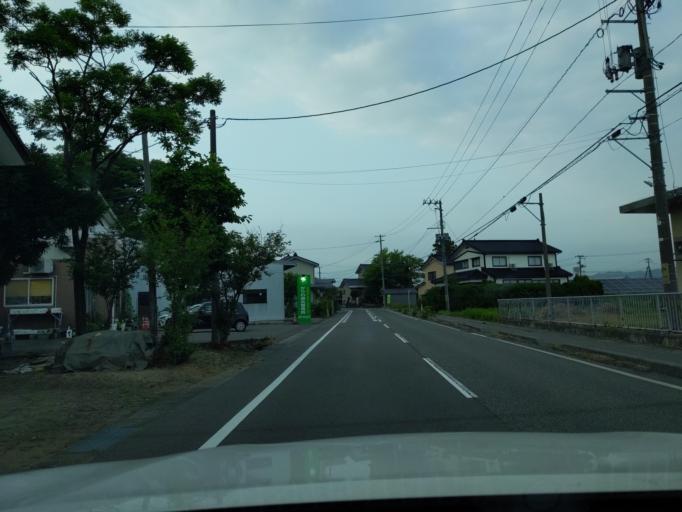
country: JP
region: Niigata
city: Kashiwazaki
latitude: 37.4208
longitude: 138.6169
